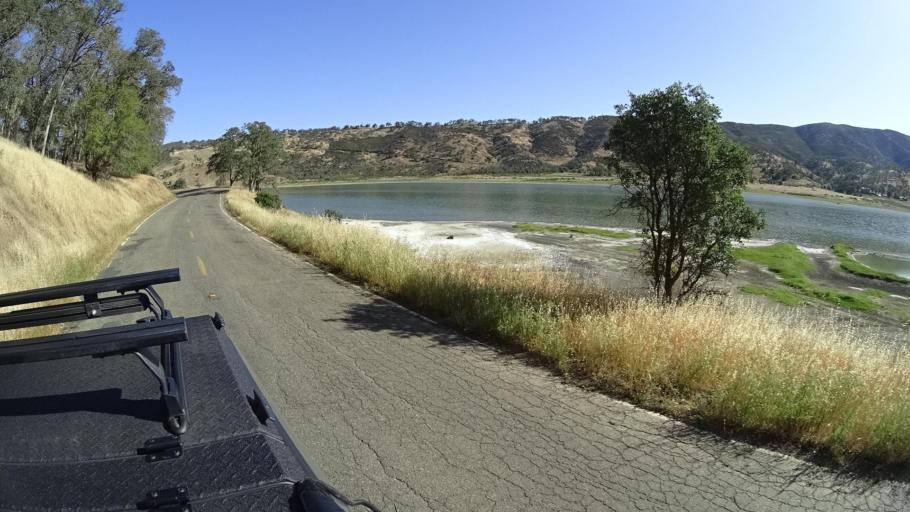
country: US
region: California
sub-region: Lake County
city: Clearlake Oaks
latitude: 38.9844
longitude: -122.6760
